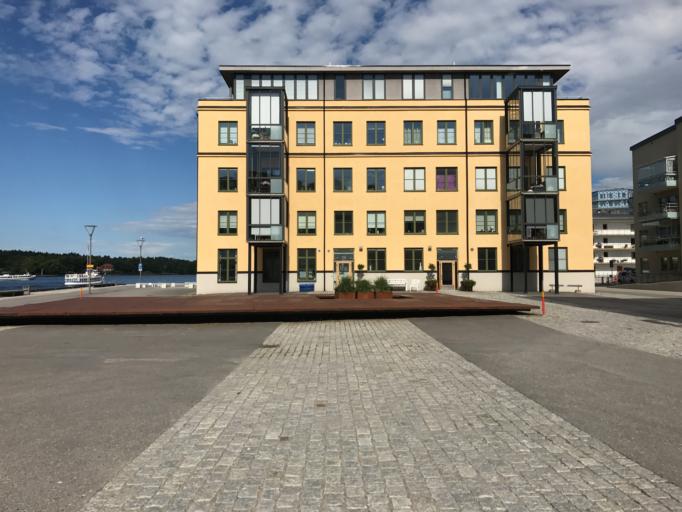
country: SE
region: Stockholm
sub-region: Nacka Kommun
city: Nacka
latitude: 59.3157
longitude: 18.1250
